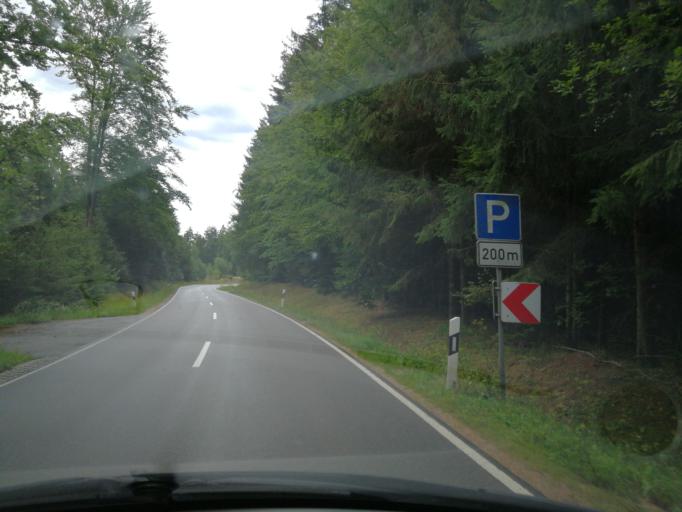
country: DE
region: Bavaria
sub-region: Upper Palatinate
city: Wiesent
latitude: 49.0381
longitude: 12.3710
